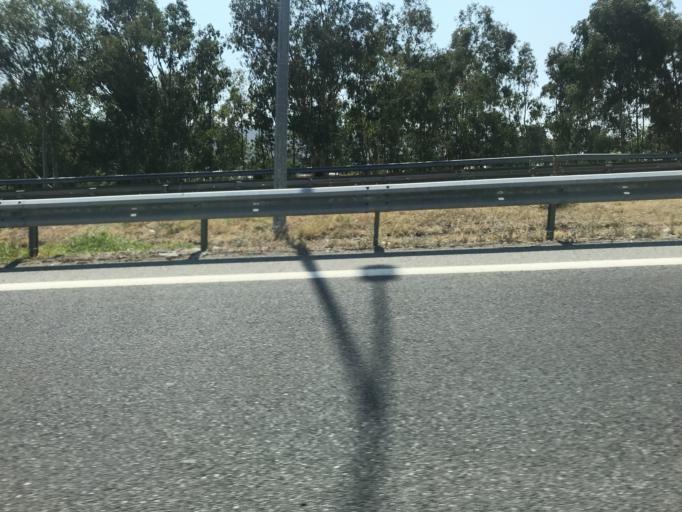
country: TR
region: Izmir
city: Urla
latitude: 38.3514
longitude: 26.8530
